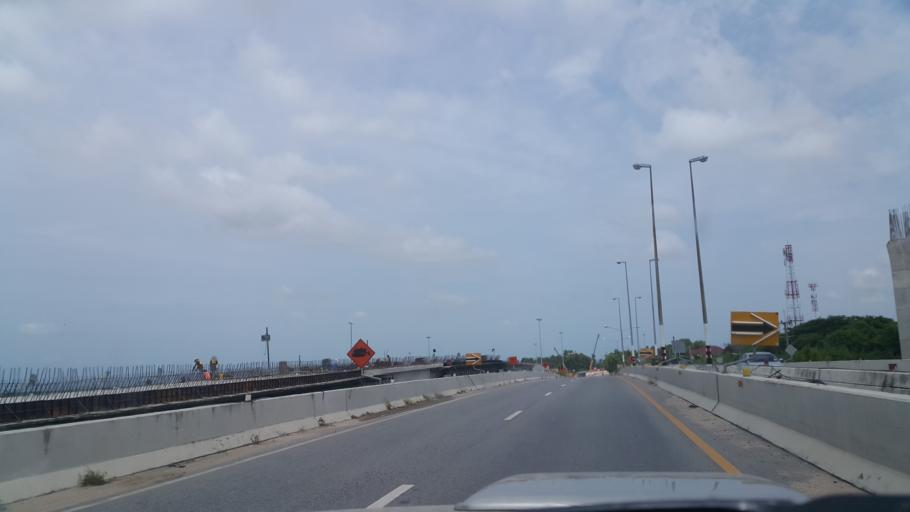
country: TH
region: Rayong
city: Ban Chang
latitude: 12.7129
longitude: 101.0318
